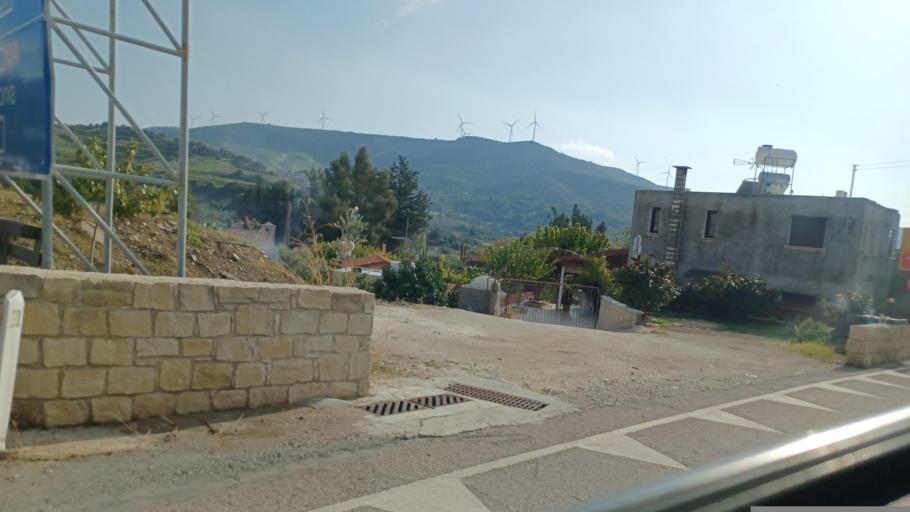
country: CY
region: Limassol
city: Pissouri
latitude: 34.7707
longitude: 32.6374
